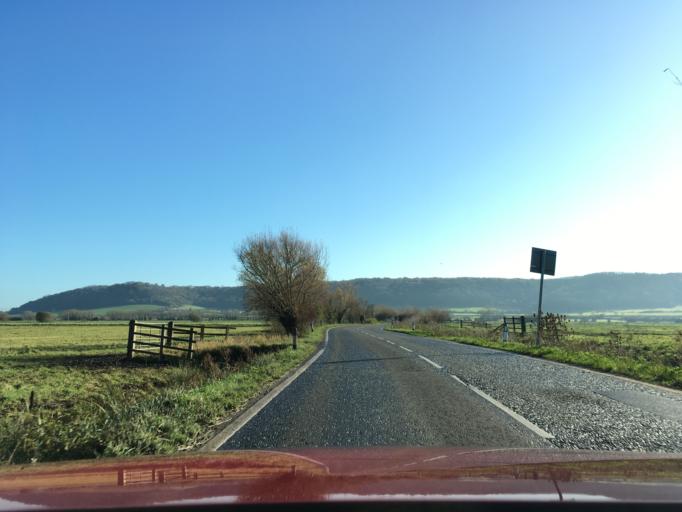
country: GB
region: England
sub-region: Somerset
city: Curry Rivel
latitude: 51.0794
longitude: -2.8668
